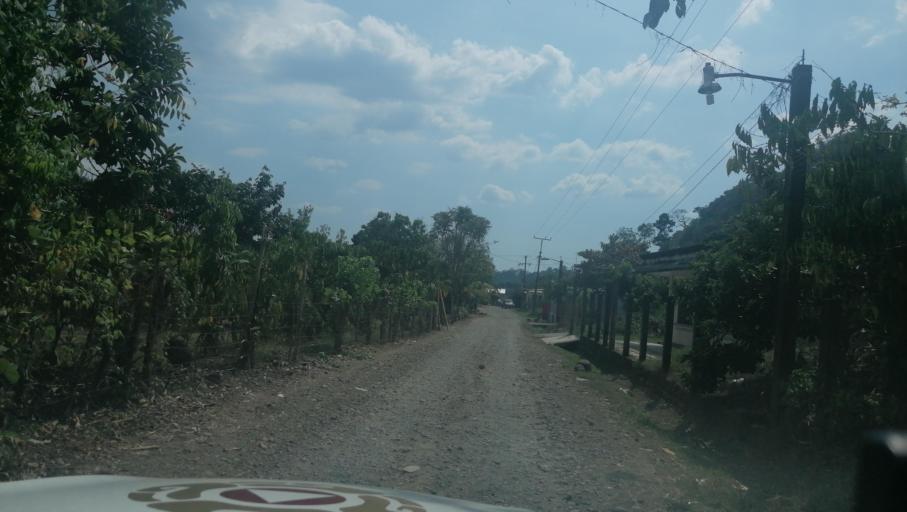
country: MX
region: Chiapas
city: Veinte de Noviembre
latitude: 15.0221
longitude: -92.2391
